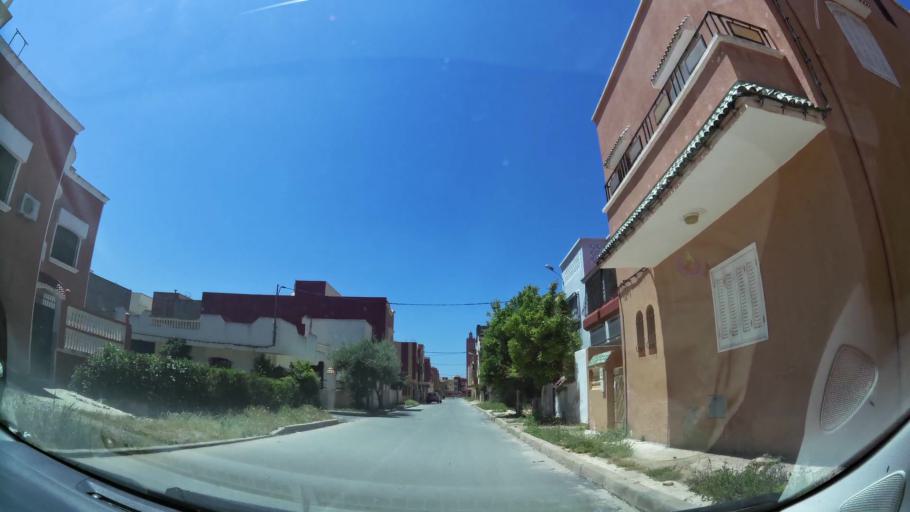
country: MA
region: Oriental
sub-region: Berkane-Taourirt
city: Madagh
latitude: 35.0802
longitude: -2.2202
